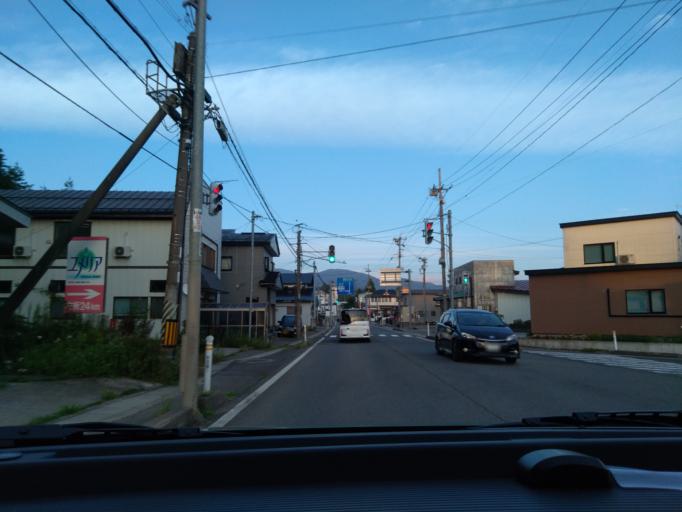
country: JP
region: Akita
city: Kakunodatemachi
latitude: 39.5919
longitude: 140.5507
